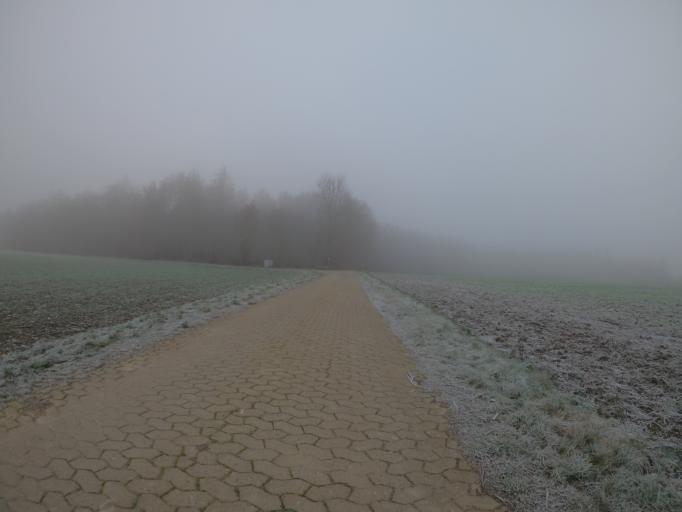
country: DE
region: Baden-Wuerttemberg
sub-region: Tuebingen Region
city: Beimerstetten
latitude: 48.4876
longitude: 9.9738
